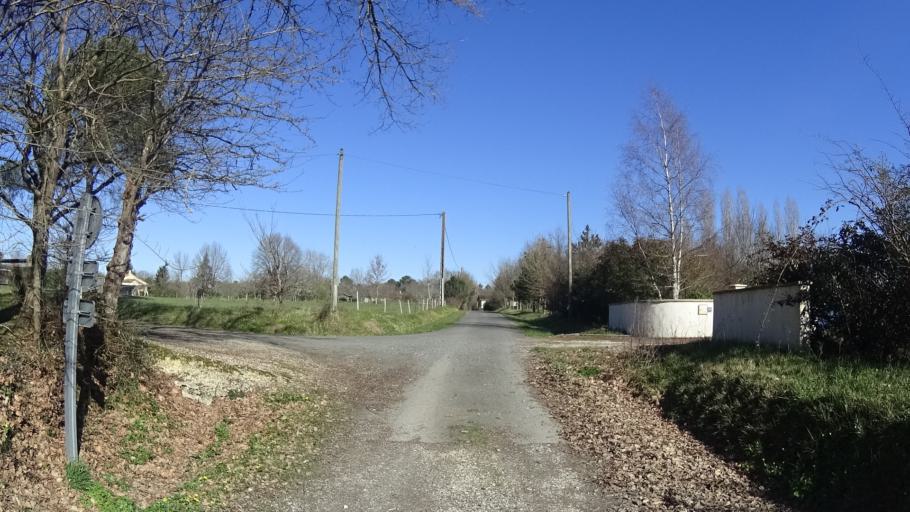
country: FR
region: Aquitaine
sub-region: Departement de la Dordogne
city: Saint-Aulaye
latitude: 45.2219
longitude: 0.1169
